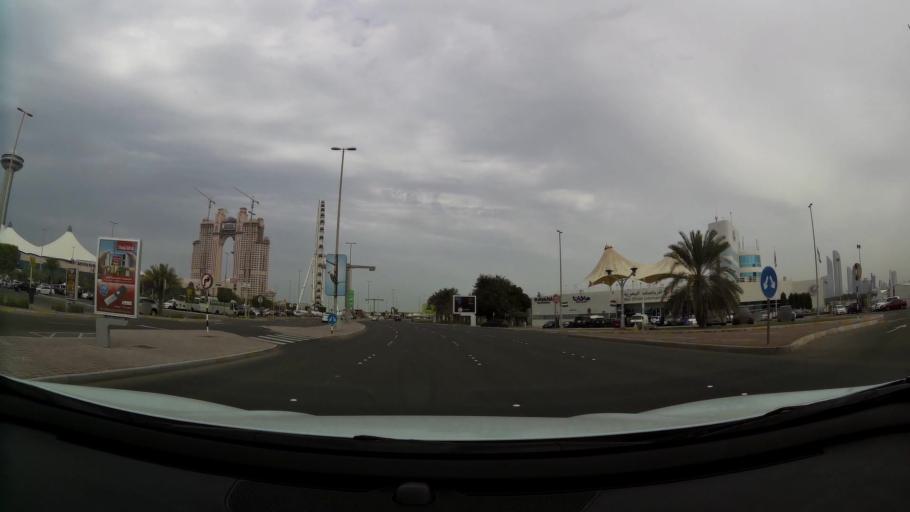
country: AE
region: Abu Dhabi
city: Abu Dhabi
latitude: 24.4737
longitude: 54.3235
